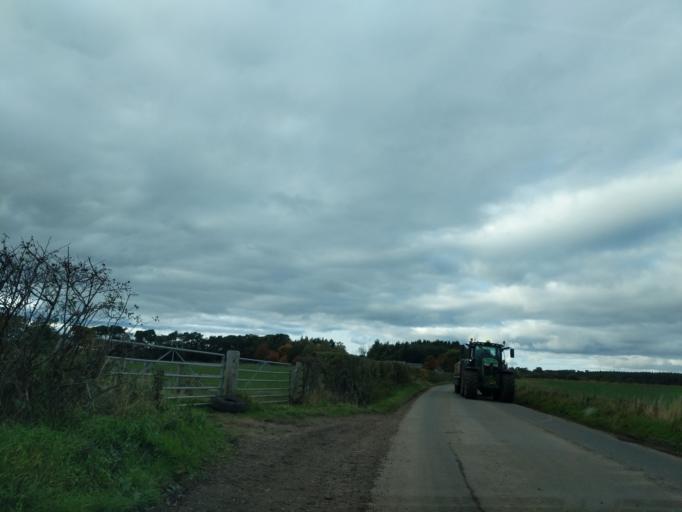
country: GB
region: Scotland
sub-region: East Lothian
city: Haddington
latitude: 55.9374
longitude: -2.8386
